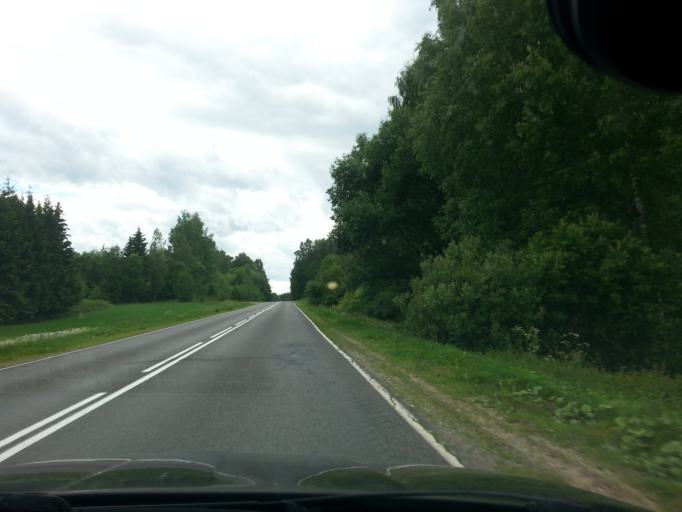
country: BY
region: Minsk
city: Svir
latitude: 54.8758
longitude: 26.3594
